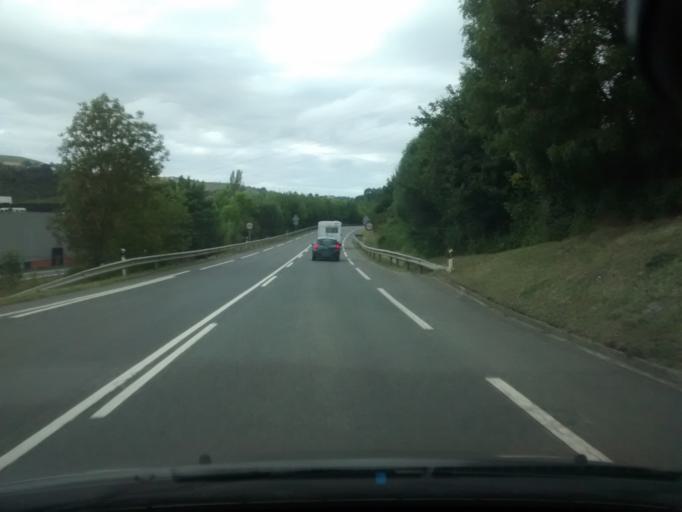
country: ES
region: Basque Country
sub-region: Provincia de Guipuzcoa
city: Zumaia
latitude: 43.2721
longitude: -2.2689
